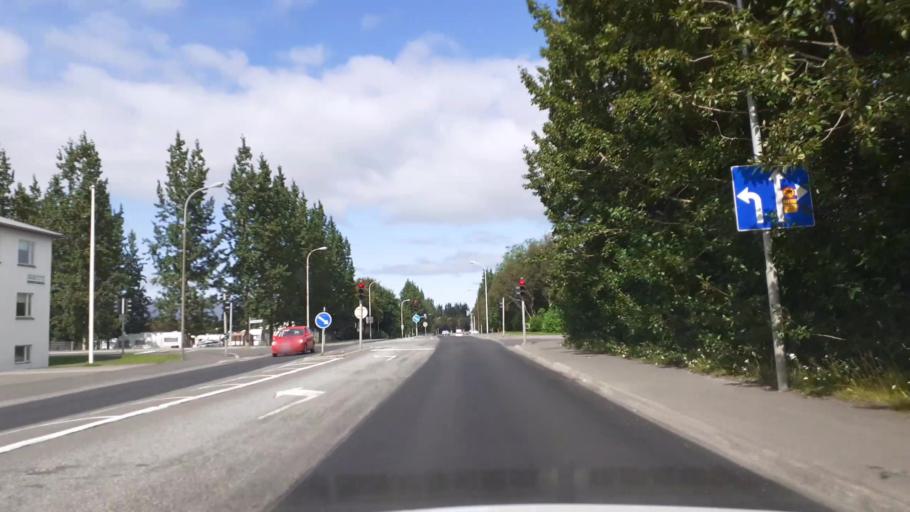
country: IS
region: Northeast
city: Akureyri
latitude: 65.6766
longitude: -18.0981
